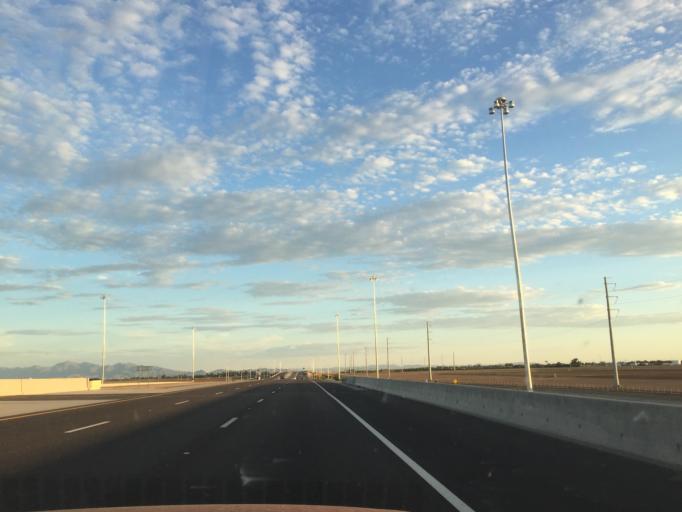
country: US
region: Arizona
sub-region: Maricopa County
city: Citrus Park
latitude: 33.5811
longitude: -112.4184
